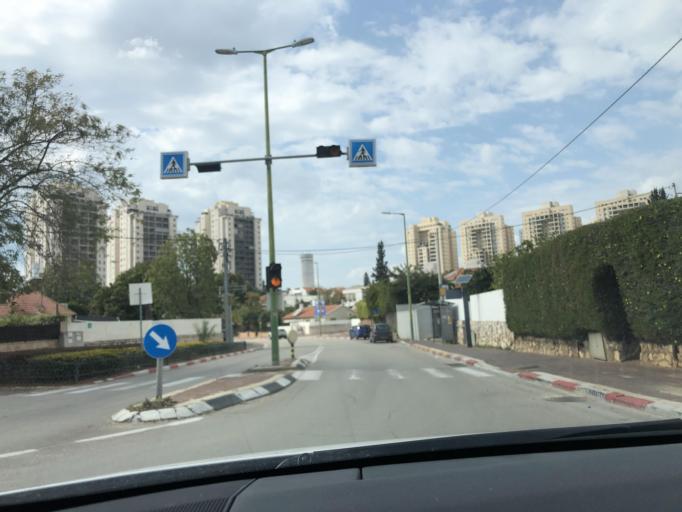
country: IL
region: Central District
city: Ganne Tiqwa
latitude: 32.0614
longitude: 34.8656
